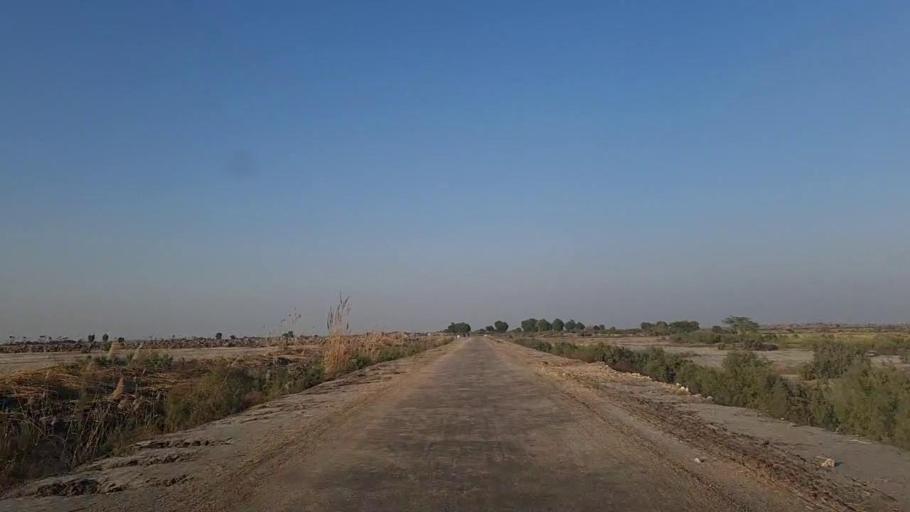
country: PK
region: Sindh
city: Jam Sahib
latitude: 26.3293
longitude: 68.6671
